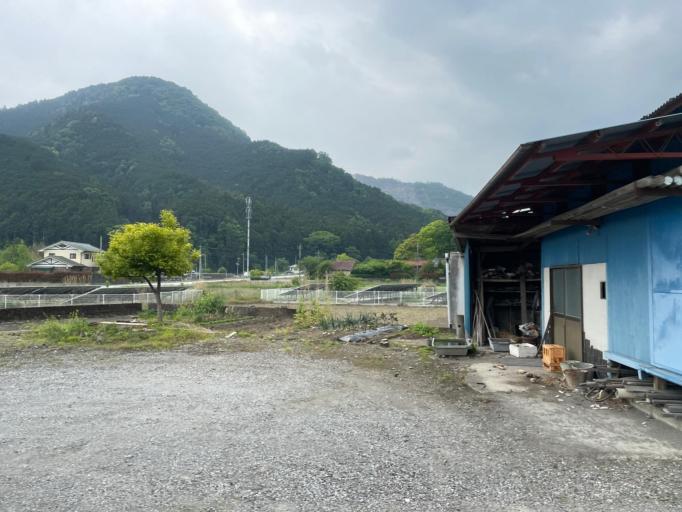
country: JP
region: Tochigi
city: Tanuma
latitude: 36.4530
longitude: 139.6390
